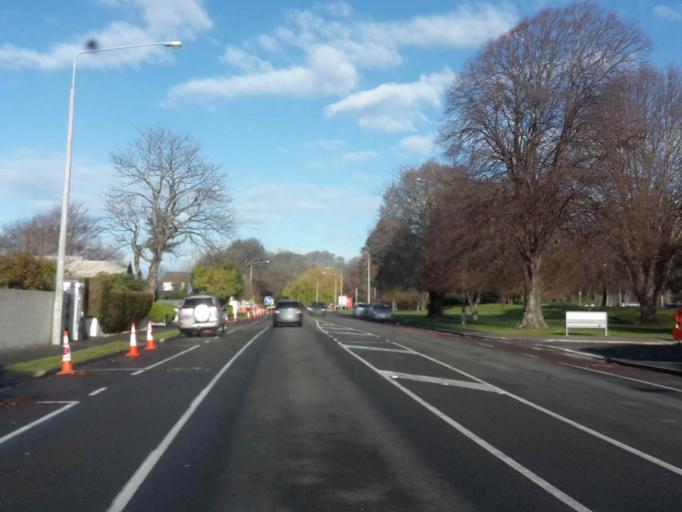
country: NZ
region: Canterbury
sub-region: Christchurch City
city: Christchurch
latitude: -43.5243
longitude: 172.5884
